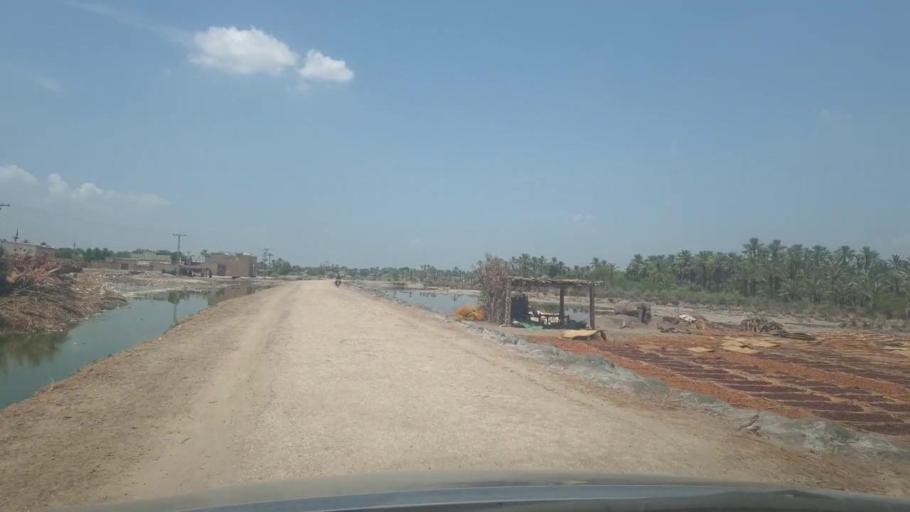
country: PK
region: Sindh
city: Kot Diji
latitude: 27.4136
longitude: 68.7374
